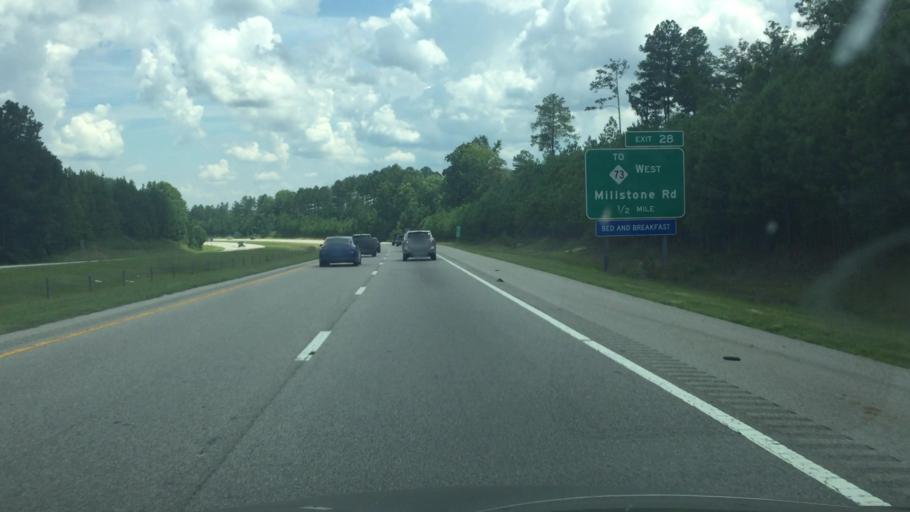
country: US
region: North Carolina
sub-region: Richmond County
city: Ellerbe
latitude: 35.0605
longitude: -79.7436
